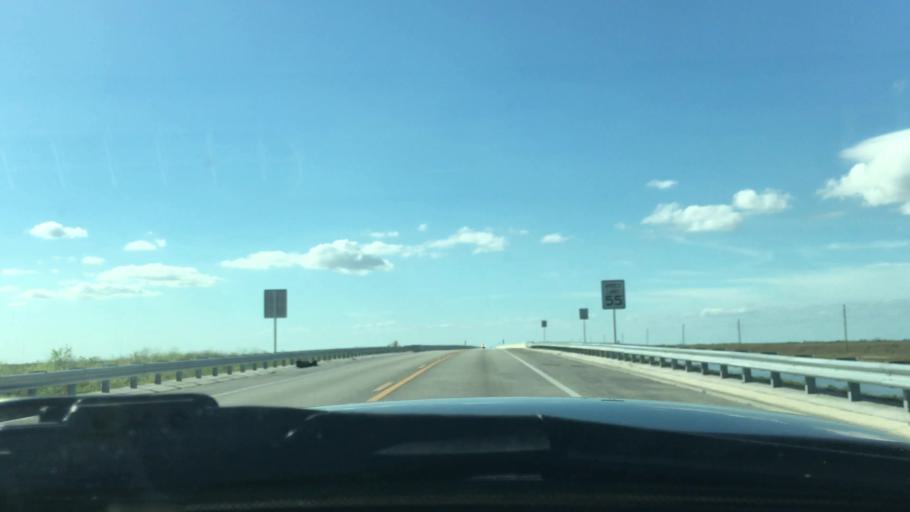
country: US
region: Florida
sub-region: Miami-Dade County
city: Kendall West
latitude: 25.7607
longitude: -80.5175
